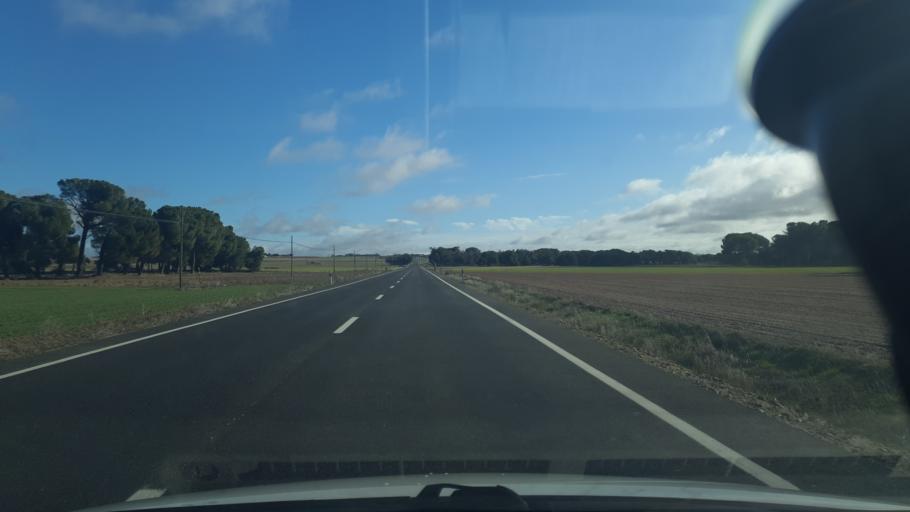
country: ES
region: Castille and Leon
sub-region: Provincia de Segovia
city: Martin Munoz de la Dehesa
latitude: 41.0466
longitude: -4.6562
